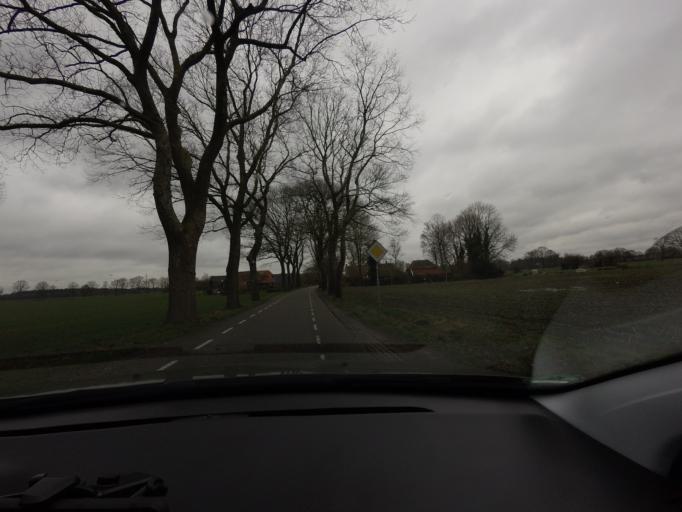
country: NL
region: Drenthe
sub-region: Gemeente Hoogeveen
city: Hoogeveen
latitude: 52.8099
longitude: 6.5172
